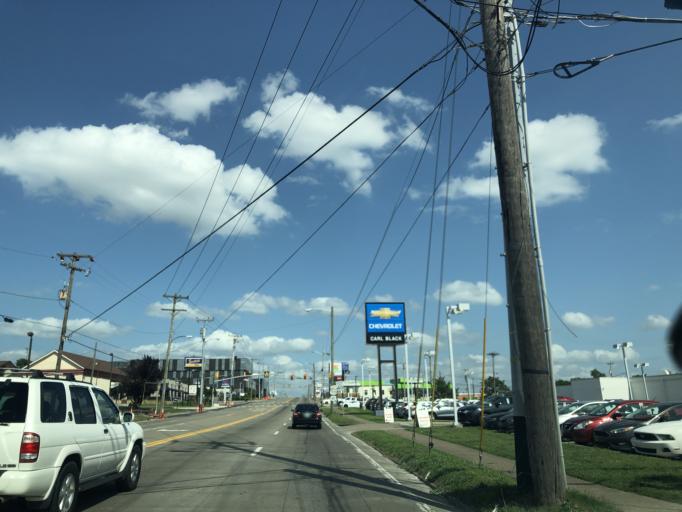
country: US
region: Tennessee
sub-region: Davidson County
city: Nashville
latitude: 36.1427
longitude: -86.7442
